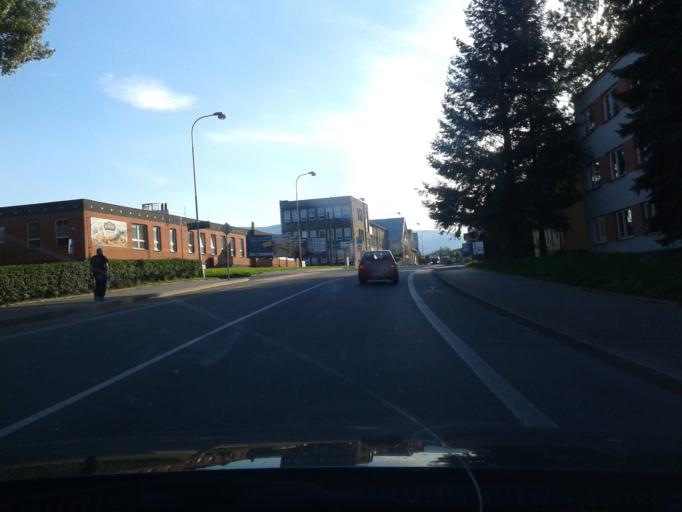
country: CZ
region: Moravskoslezsky
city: Trinec
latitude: 49.6779
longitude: 18.6652
